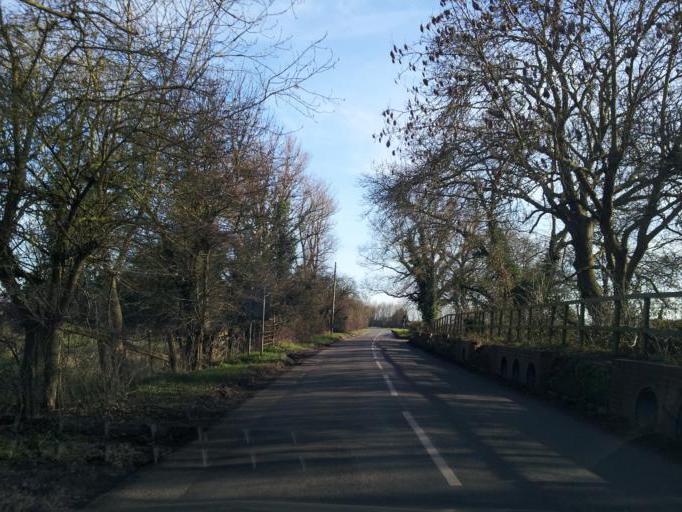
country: GB
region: England
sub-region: Cambridgeshire
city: Meldreth
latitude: 52.1218
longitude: 0.0225
